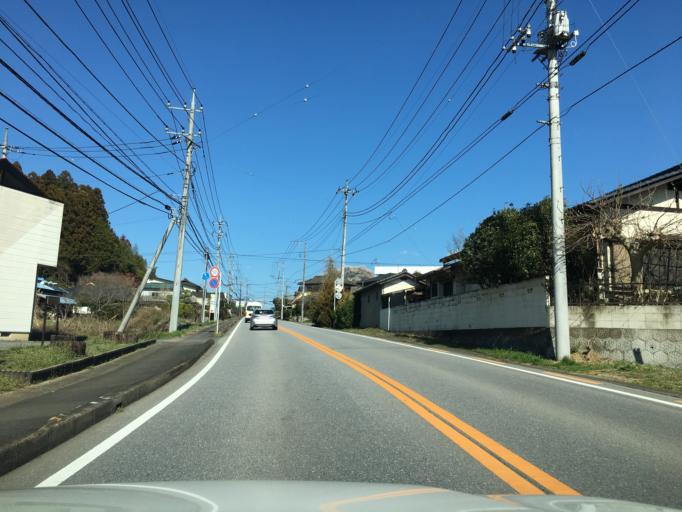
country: JP
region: Tochigi
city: Motegi
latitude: 36.5417
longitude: 140.2153
